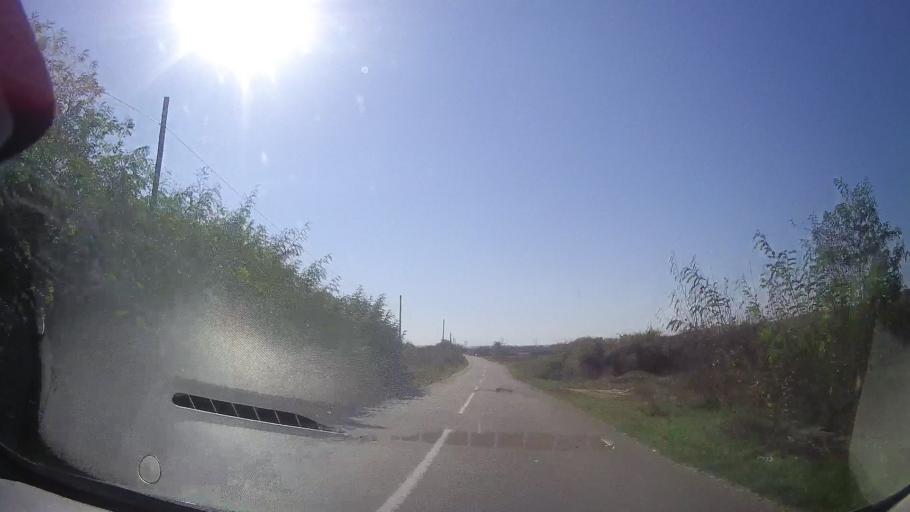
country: RO
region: Timis
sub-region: Comuna Bethausen
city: Bethausen
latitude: 45.8530
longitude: 21.9656
